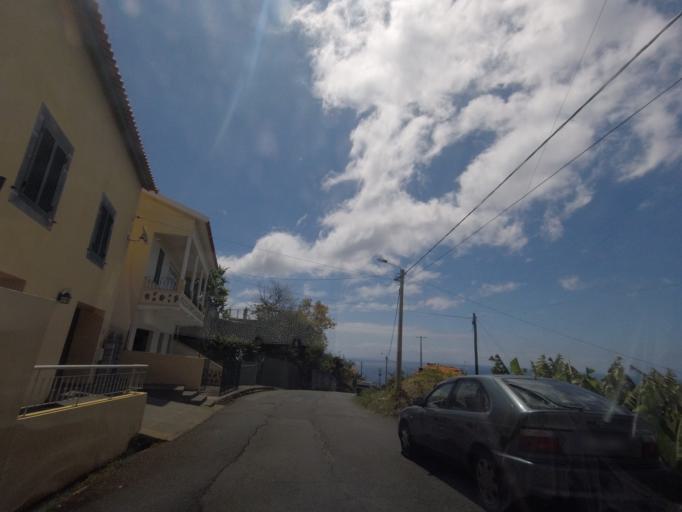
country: PT
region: Madeira
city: Ponta do Sol
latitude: 32.6816
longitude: -17.0829
